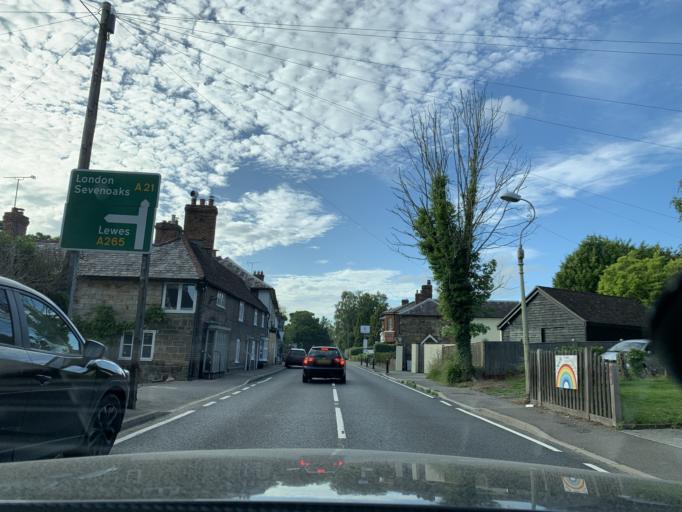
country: GB
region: England
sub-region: East Sussex
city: Robertsbridge
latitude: 51.0165
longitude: 0.4712
